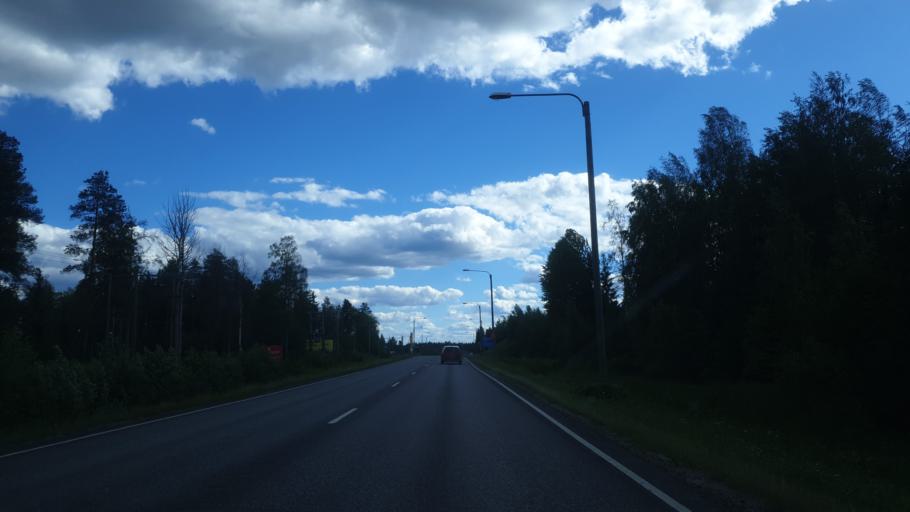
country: FI
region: Southern Savonia
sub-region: Pieksaemaeki
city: Juva
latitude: 61.9054
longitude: 27.8046
